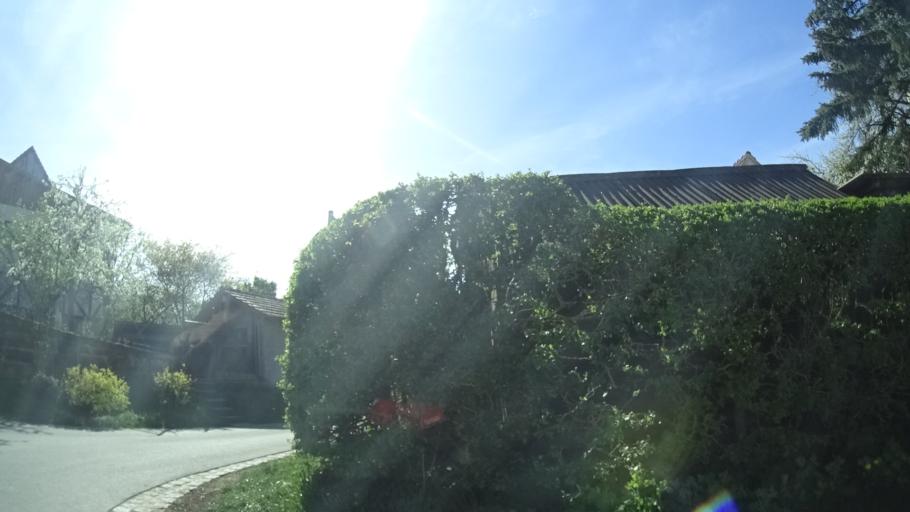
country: DE
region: Bavaria
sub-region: Regierungsbezirk Unterfranken
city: Burgpreppach
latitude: 50.0988
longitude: 10.6625
